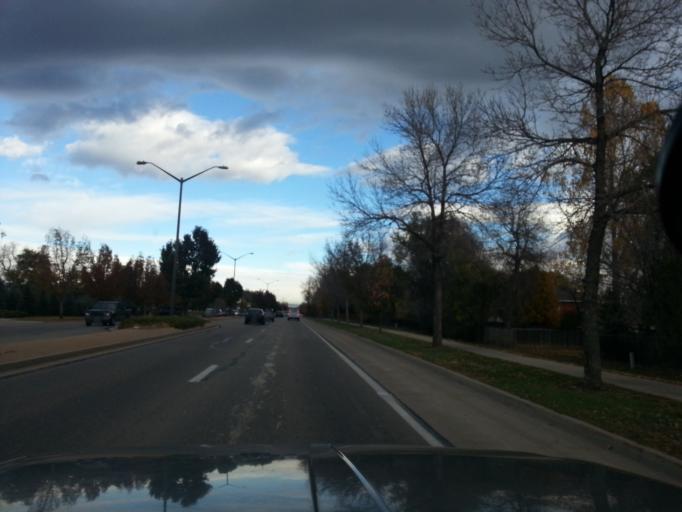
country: US
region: Colorado
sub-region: Larimer County
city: Fort Collins
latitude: 40.5439
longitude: -105.1151
